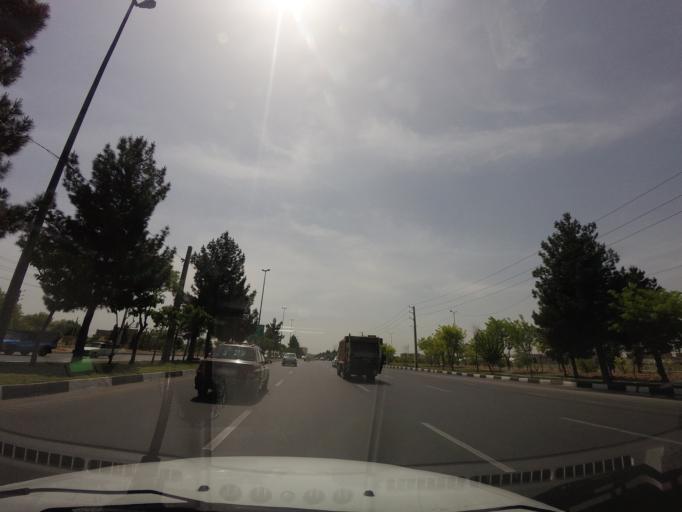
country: IR
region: Tehran
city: Eslamshahr
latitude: 35.5590
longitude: 51.2547
